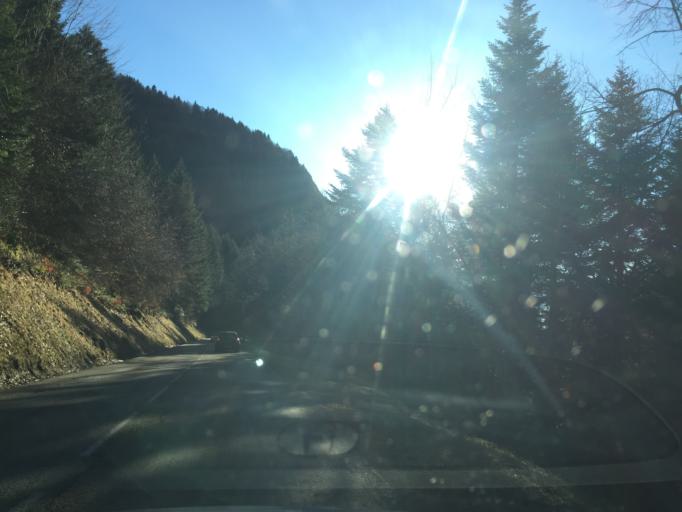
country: FR
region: Rhone-Alpes
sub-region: Departement de la Savoie
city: Mouxy
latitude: 45.7039
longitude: 5.9965
